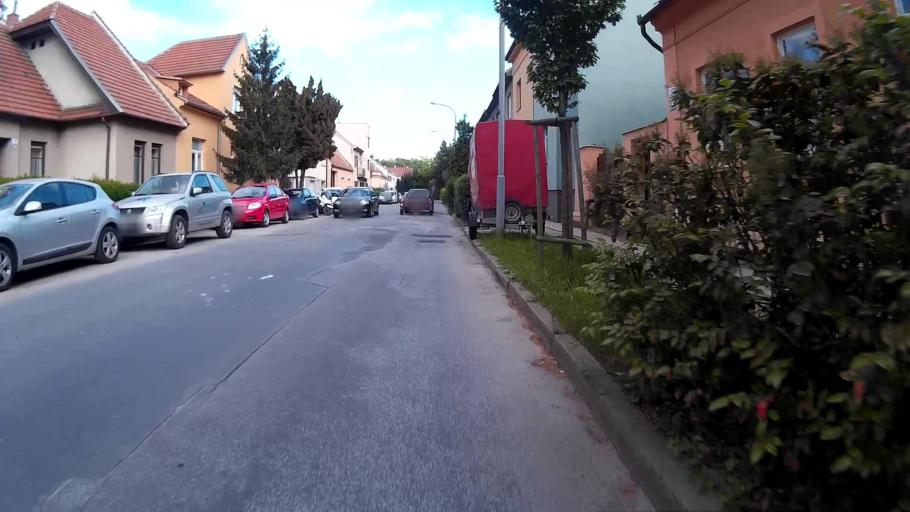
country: CZ
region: South Moravian
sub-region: Mesto Brno
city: Brno
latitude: 49.2128
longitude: 16.5713
